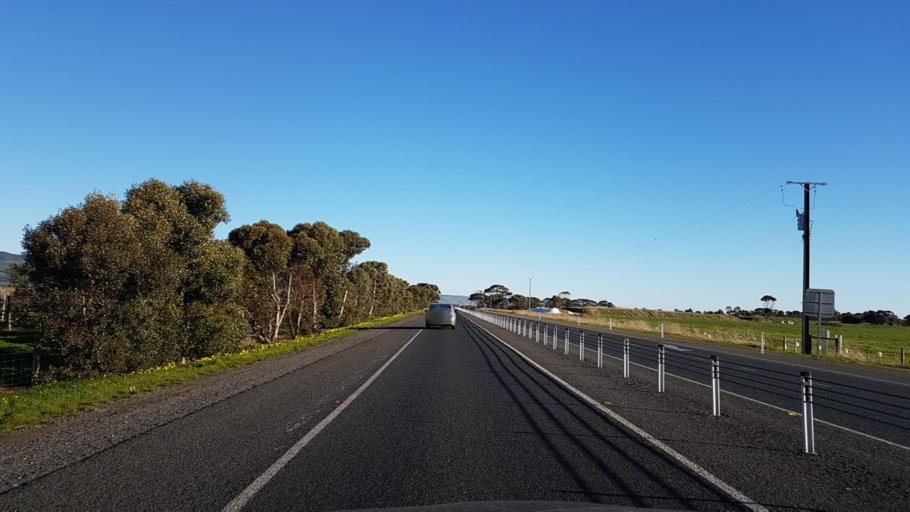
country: AU
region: South Australia
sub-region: Onkaparinga
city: Aldinga
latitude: -35.2573
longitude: 138.4924
